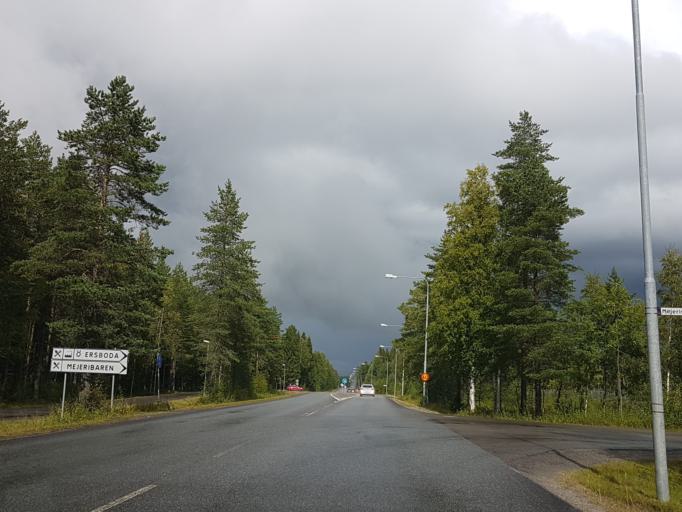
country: SE
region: Vaesterbotten
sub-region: Umea Kommun
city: Ersmark
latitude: 63.8510
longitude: 20.3435
